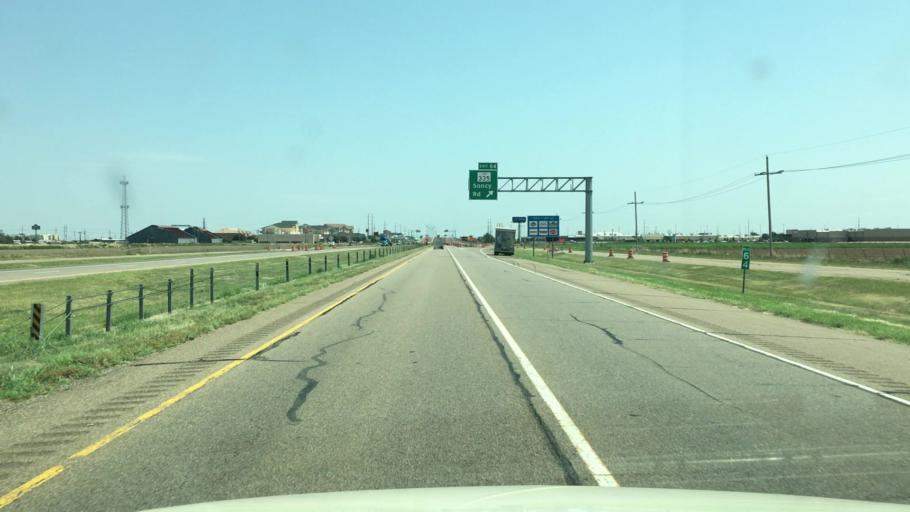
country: US
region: Texas
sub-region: Potter County
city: Bushland
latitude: 35.1873
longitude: -101.9491
